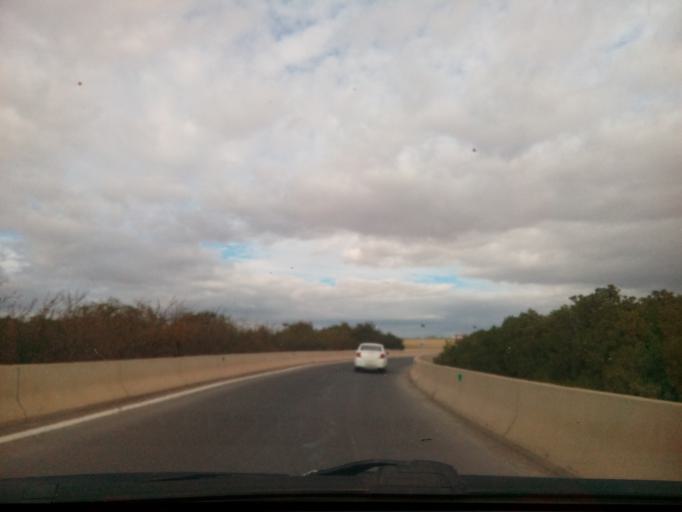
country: DZ
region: Sidi Bel Abbes
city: Sidi Bel Abbes
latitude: 35.2194
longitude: -0.6735
